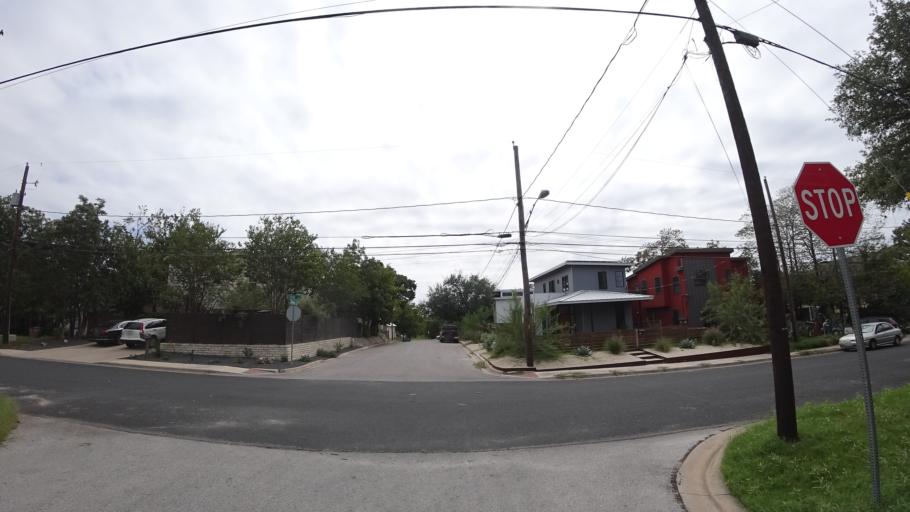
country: US
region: Texas
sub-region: Travis County
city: Austin
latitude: 30.2752
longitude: -97.7182
